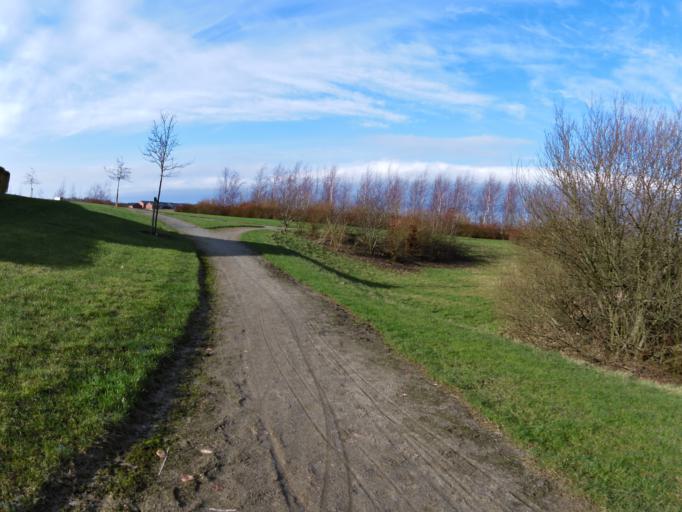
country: DK
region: Central Jutland
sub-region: Arhus Kommune
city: Stavtrup
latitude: 56.1146
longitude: 10.0991
